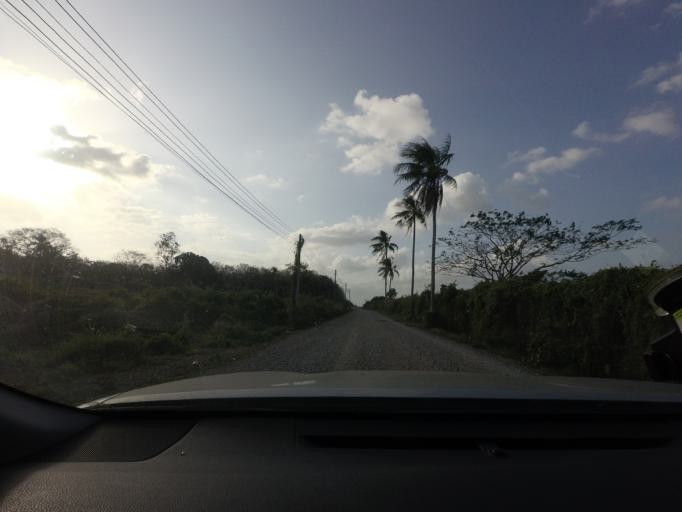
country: TH
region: Pattani
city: Mae Lan
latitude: 6.6153
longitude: 101.2567
